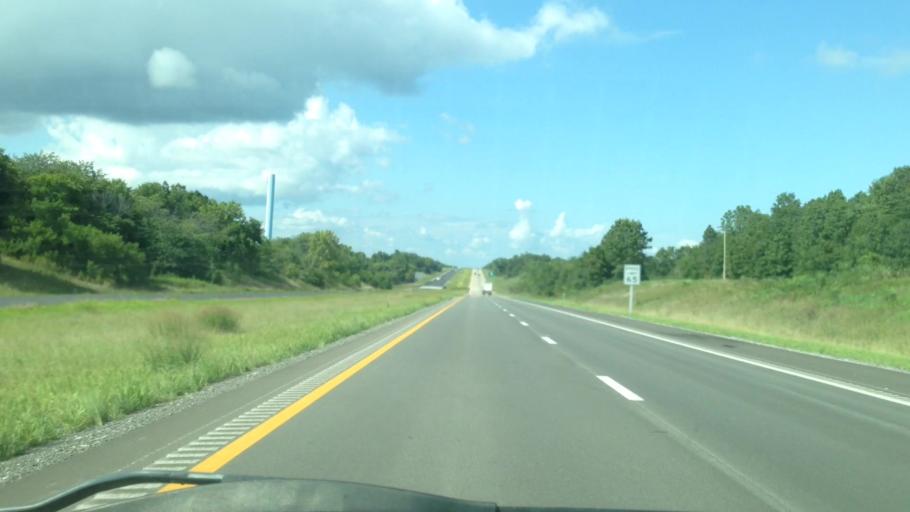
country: US
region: Missouri
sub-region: Lewis County
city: Canton
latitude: 40.0231
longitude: -91.5259
